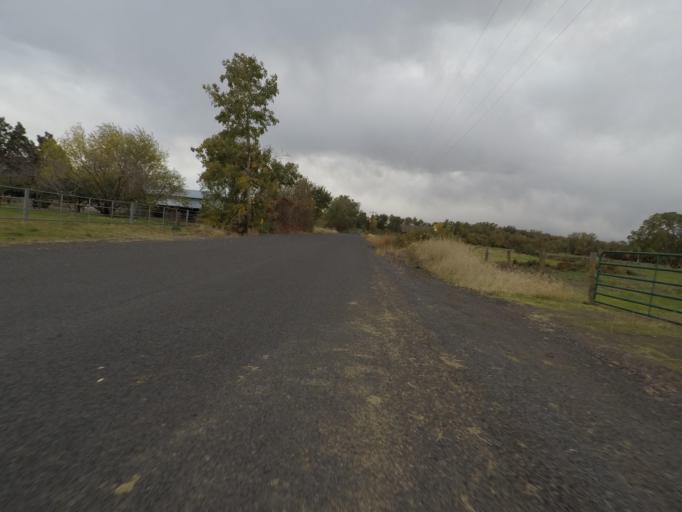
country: US
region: Washington
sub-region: Walla Walla County
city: Walla Walla East
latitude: 46.0858
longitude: -118.2525
